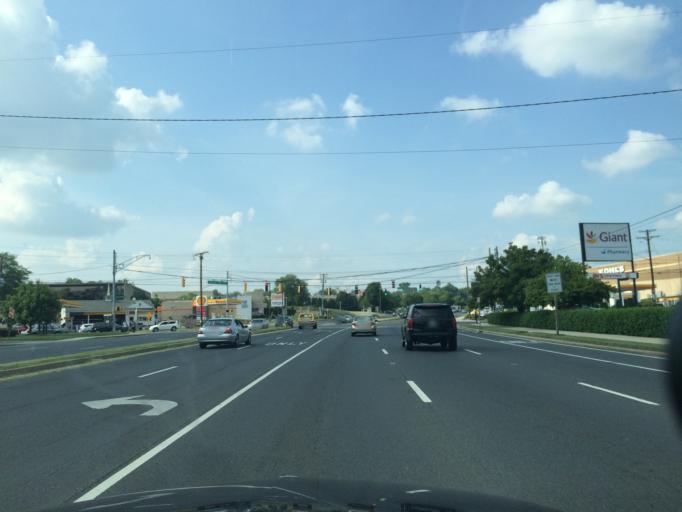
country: US
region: Maryland
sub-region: Montgomery County
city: Aspen Hill
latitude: 39.0793
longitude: -77.0807
